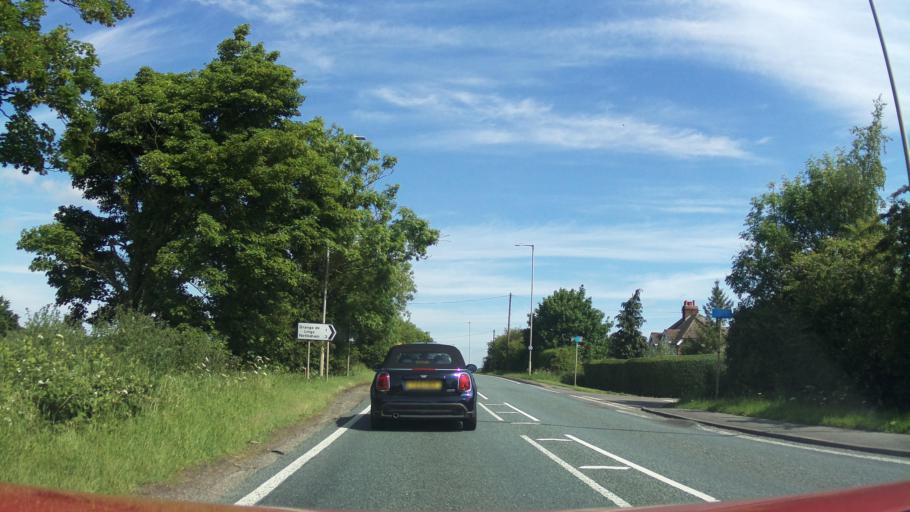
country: GB
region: England
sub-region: Lincolnshire
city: Burton
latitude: 53.2826
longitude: -0.5404
